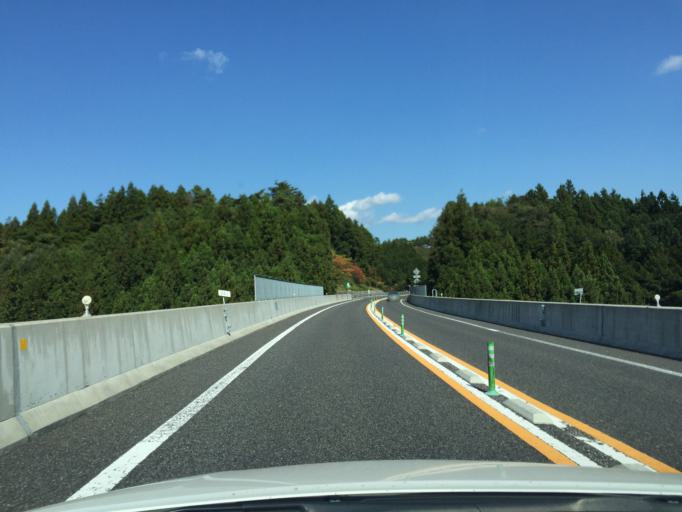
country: JP
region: Fukushima
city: Ishikawa
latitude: 37.2256
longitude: 140.5459
